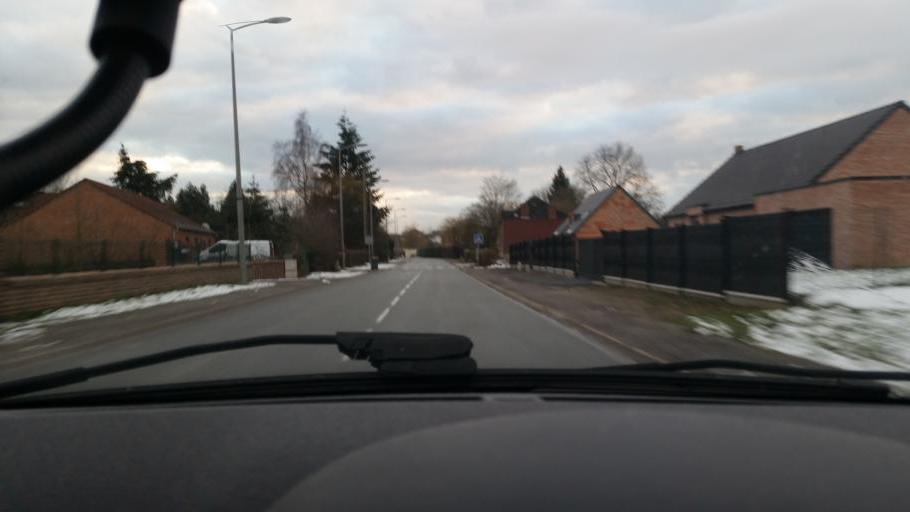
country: FR
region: Nord-Pas-de-Calais
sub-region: Departement du Nord
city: Marpent
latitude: 50.2393
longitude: 4.0949
